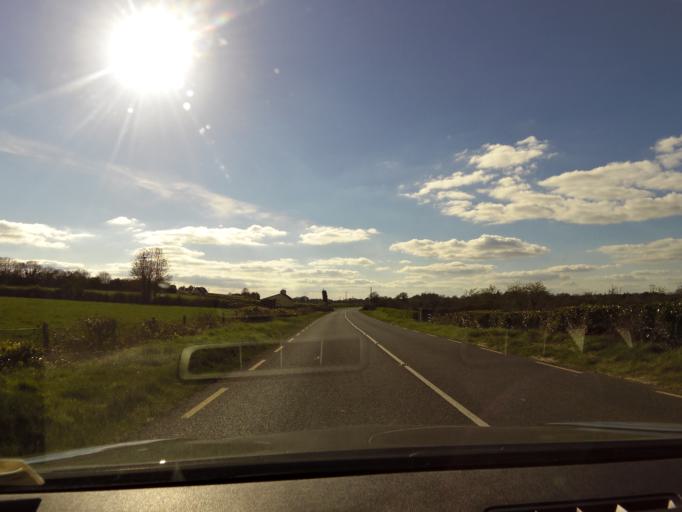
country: IE
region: Leinster
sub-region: Uibh Fhaili
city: Banagher
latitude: 53.1061
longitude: -8.0297
